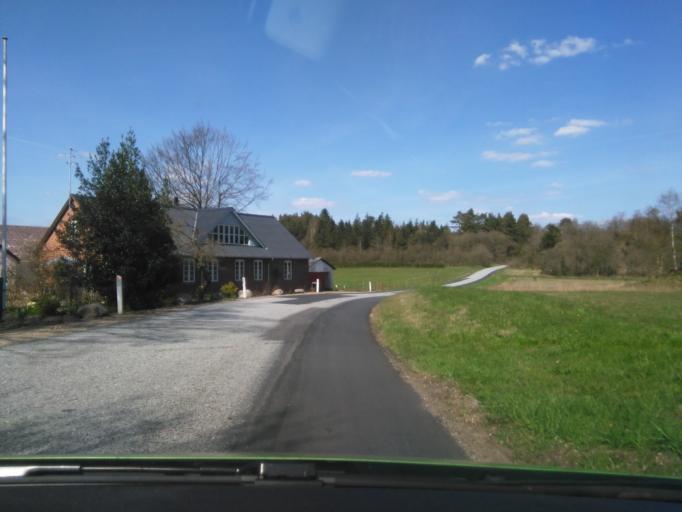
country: DK
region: Central Jutland
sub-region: Viborg Kommune
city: Viborg
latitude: 56.3754
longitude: 9.2940
